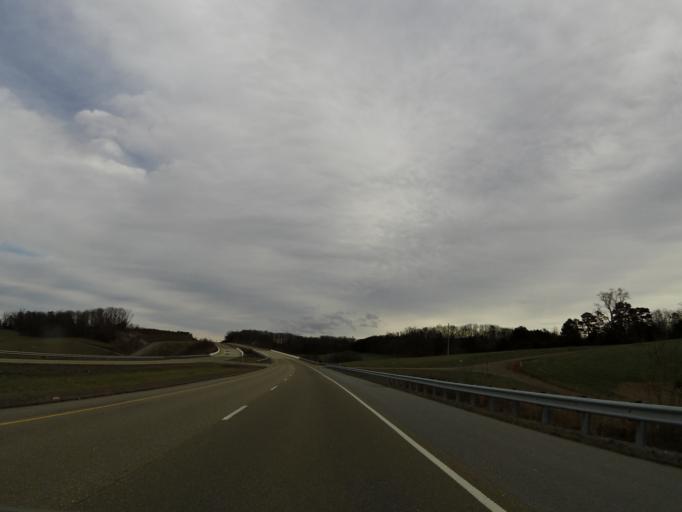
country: US
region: Tennessee
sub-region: Cocke County
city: Newport
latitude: 36.0057
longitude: -83.0713
